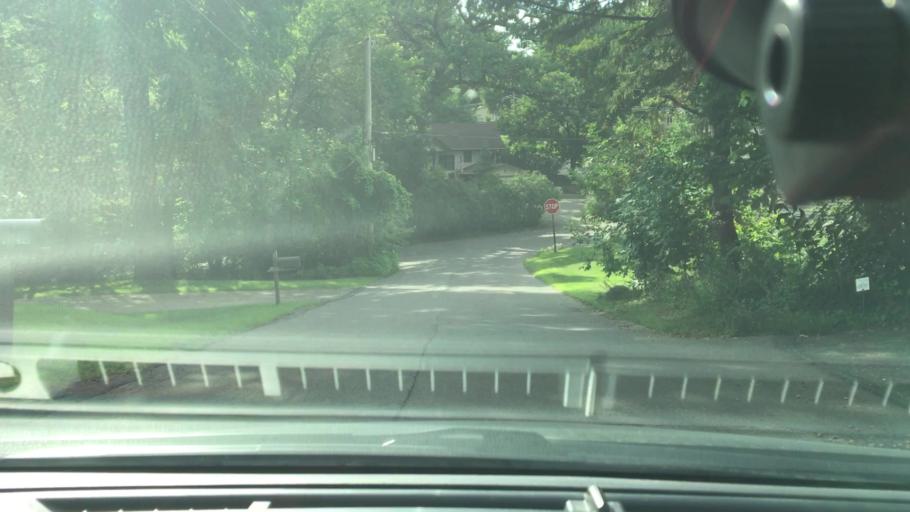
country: US
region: Minnesota
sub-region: Hennepin County
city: Plymouth
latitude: 45.0060
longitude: -93.4363
